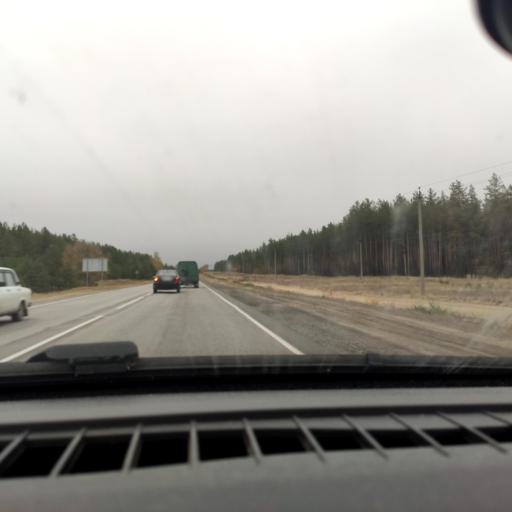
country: RU
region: Voronezj
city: Uryv-Pokrovka
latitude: 51.0512
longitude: 38.9855
